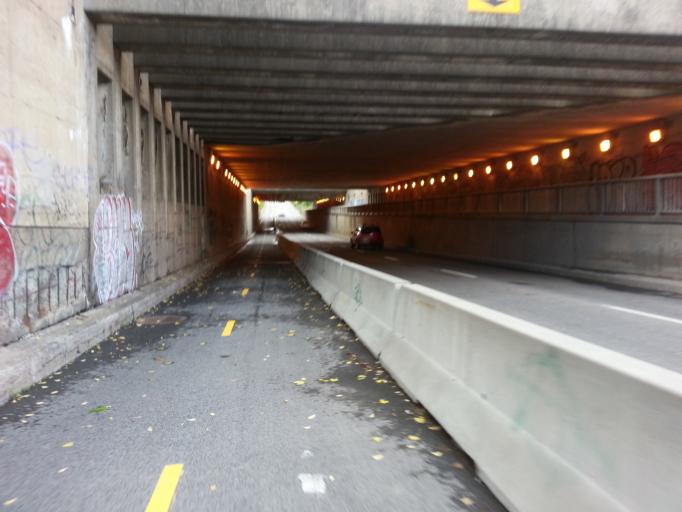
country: CA
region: Quebec
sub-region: Montreal
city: Montreal
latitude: 45.5286
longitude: -73.6072
